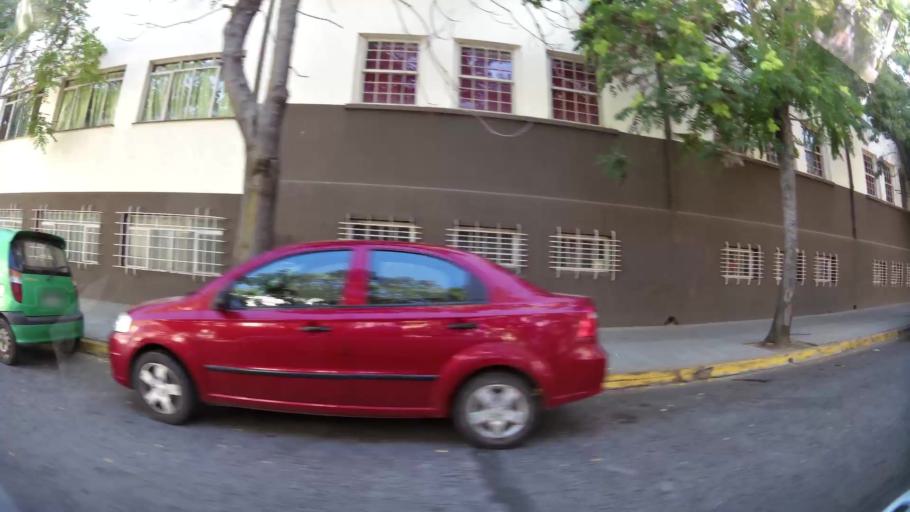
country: CL
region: Maule
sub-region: Provincia de Talca
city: Talca
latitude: -35.4233
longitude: -71.6650
